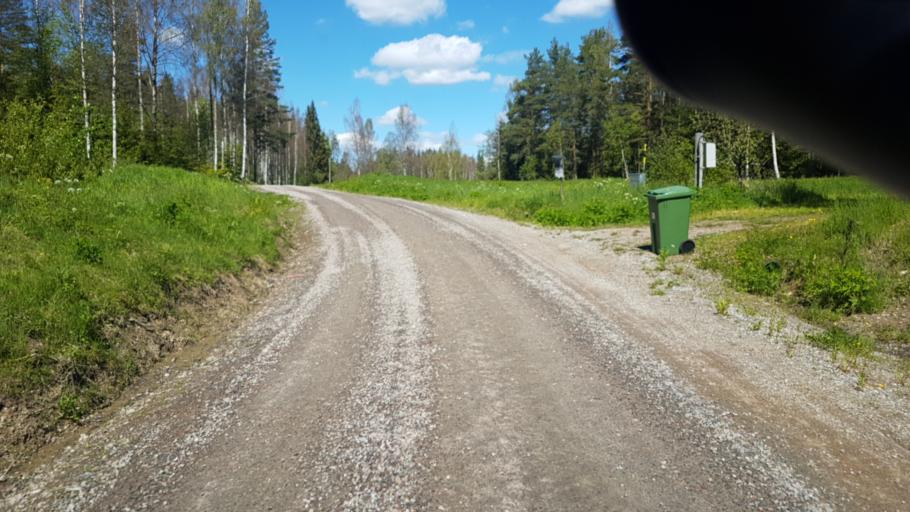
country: SE
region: Vaermland
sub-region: Arvika Kommun
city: Arvika
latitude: 59.5710
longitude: 12.8345
